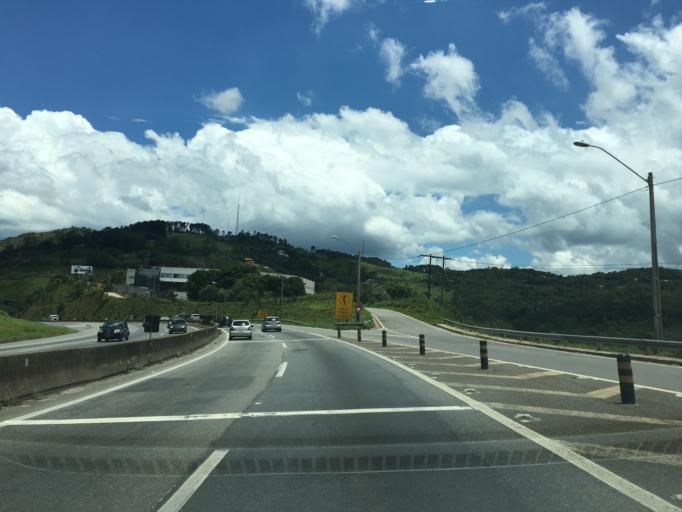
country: BR
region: Sao Paulo
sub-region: Mairipora
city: Mairipora
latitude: -23.2865
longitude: -46.5902
